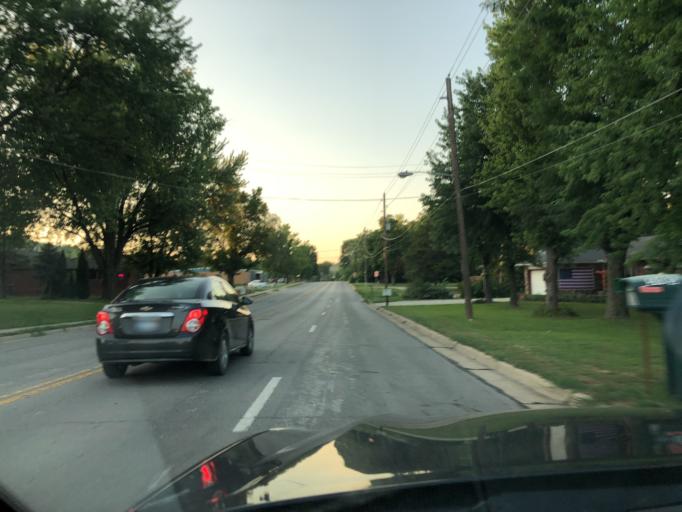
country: US
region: Kansas
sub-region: Leavenworth County
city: Leavenworth
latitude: 39.3141
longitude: -94.9506
